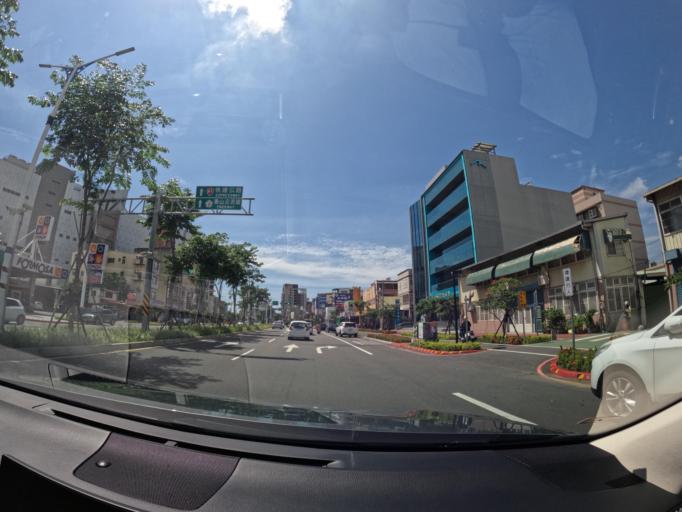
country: TW
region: Taiwan
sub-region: Hsinchu
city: Hsinchu
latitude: 24.6880
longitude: 120.9066
